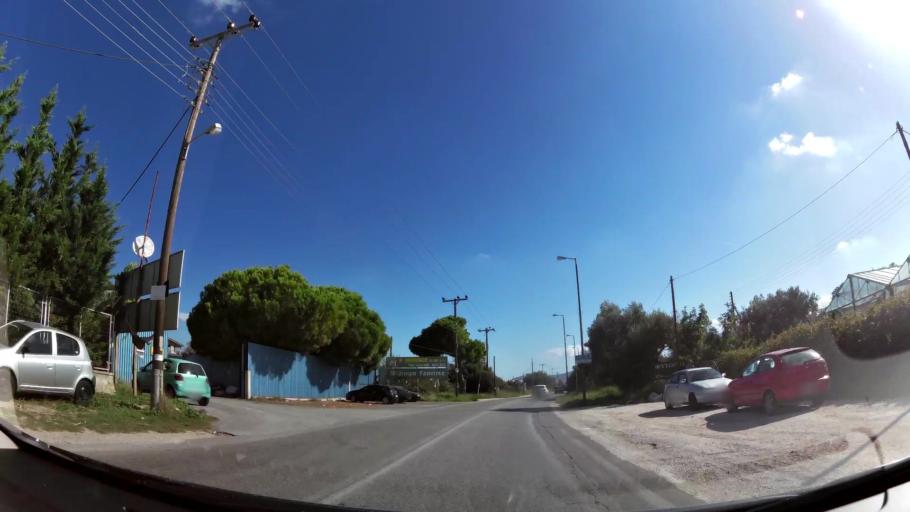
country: GR
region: Attica
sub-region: Nomarchia Anatolikis Attikis
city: Markopoulo
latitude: 37.8876
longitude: 23.9017
